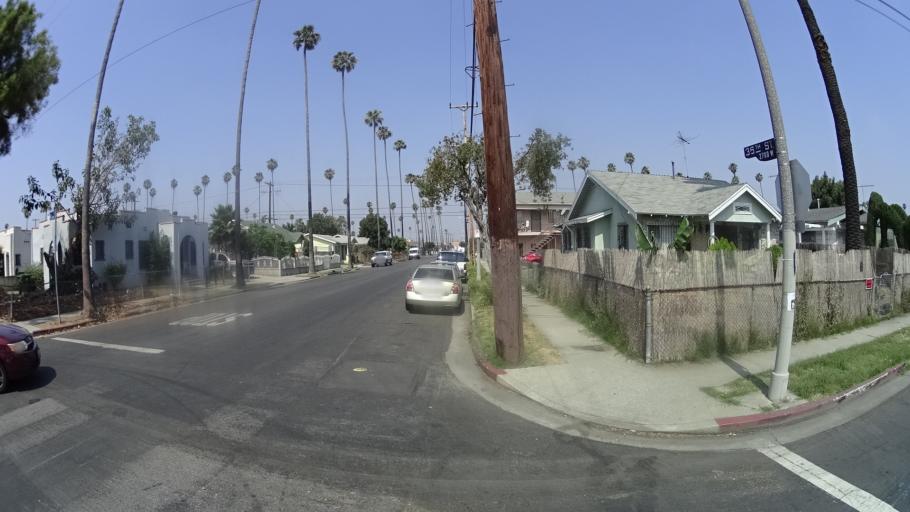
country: US
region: California
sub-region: Los Angeles County
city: View Park-Windsor Hills
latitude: 34.0231
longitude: -118.3248
